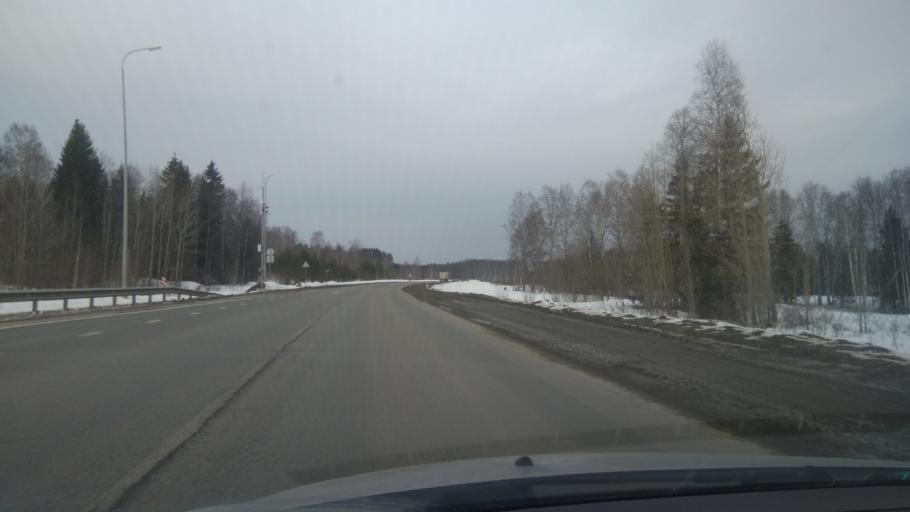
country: RU
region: Sverdlovsk
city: Ufimskiy
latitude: 56.7823
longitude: 58.3997
